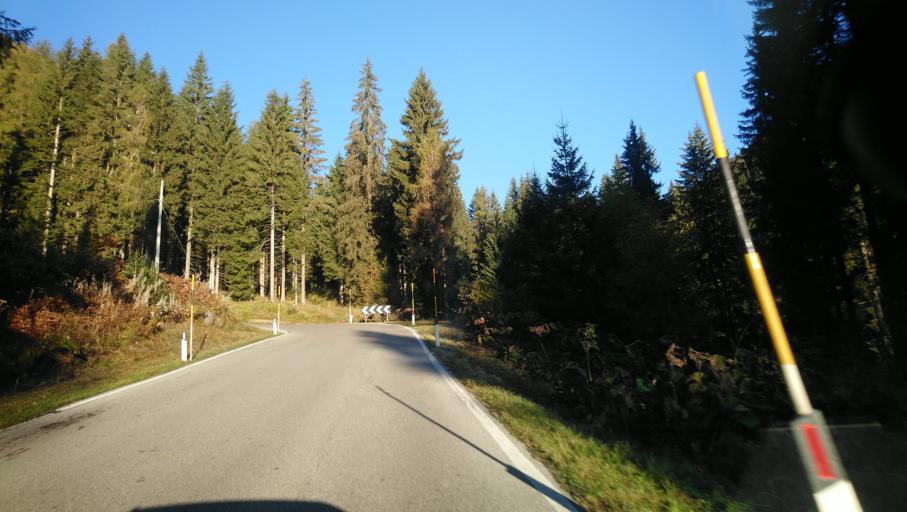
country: IT
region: Veneto
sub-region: Provincia di Belluno
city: Falcade Alto
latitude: 46.3617
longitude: 11.8414
